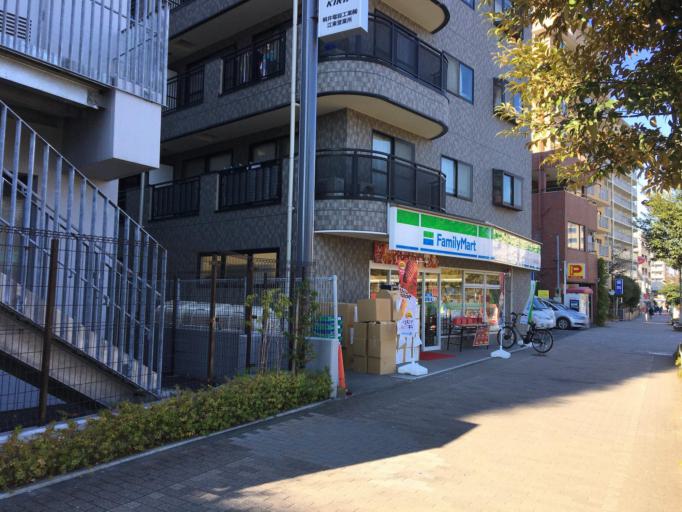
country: JP
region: Tokyo
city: Urayasu
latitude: 35.6884
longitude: 139.8450
